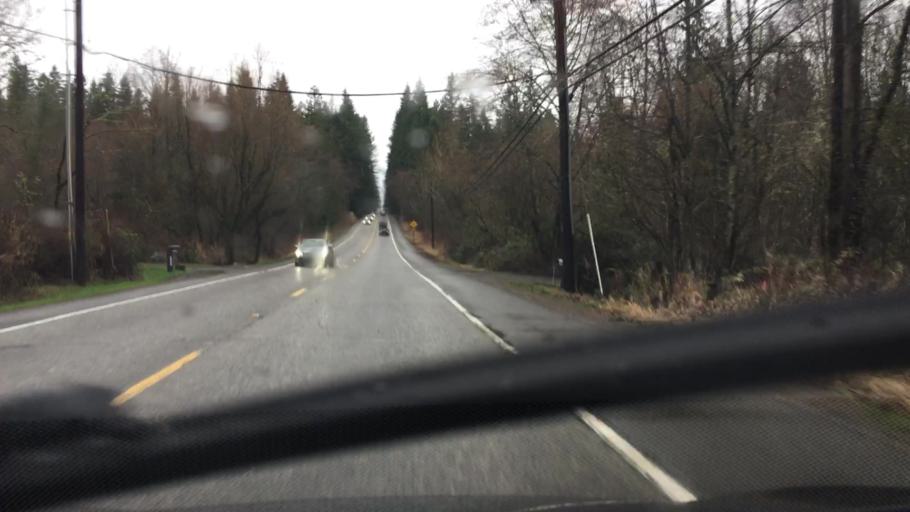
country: US
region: Washington
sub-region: King County
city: Cottage Lake
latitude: 47.7237
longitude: -122.0854
